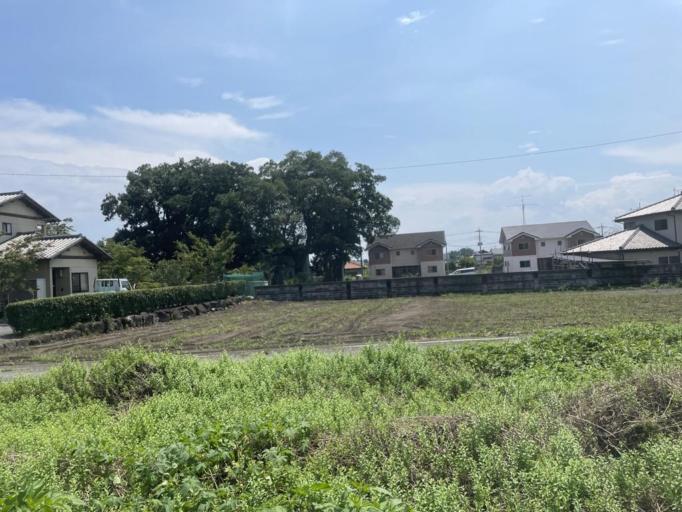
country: JP
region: Gunma
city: Omamacho-omama
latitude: 36.4138
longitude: 139.1837
